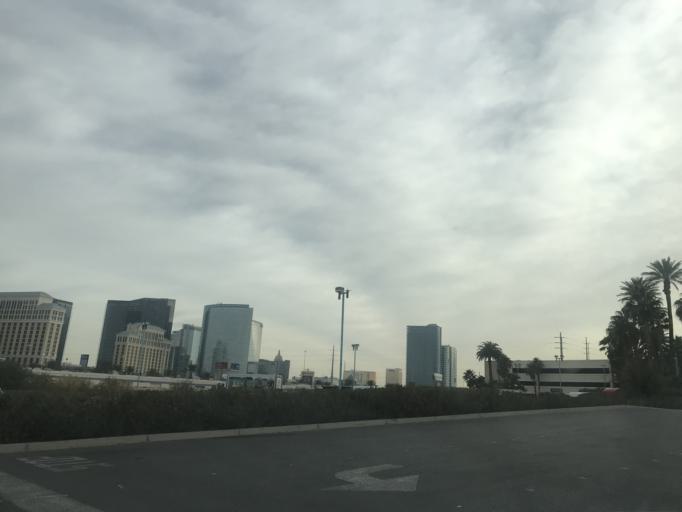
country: US
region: Nevada
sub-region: Clark County
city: Paradise
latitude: 36.1186
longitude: -115.1843
